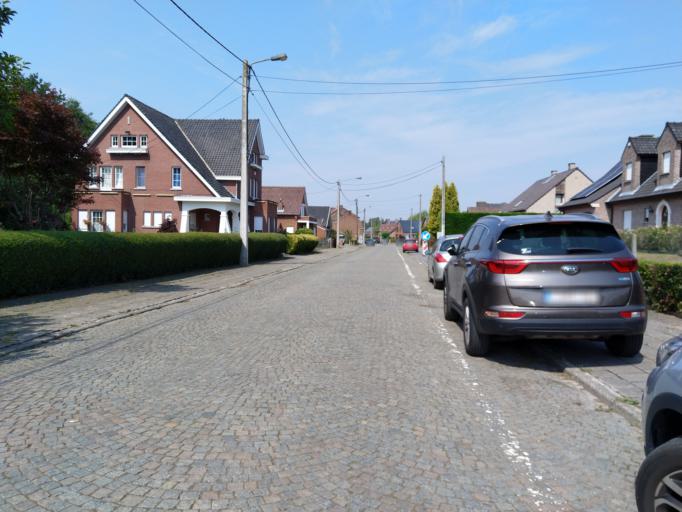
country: BE
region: Wallonia
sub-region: Province du Hainaut
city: Roeulx
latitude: 50.4766
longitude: 4.0678
